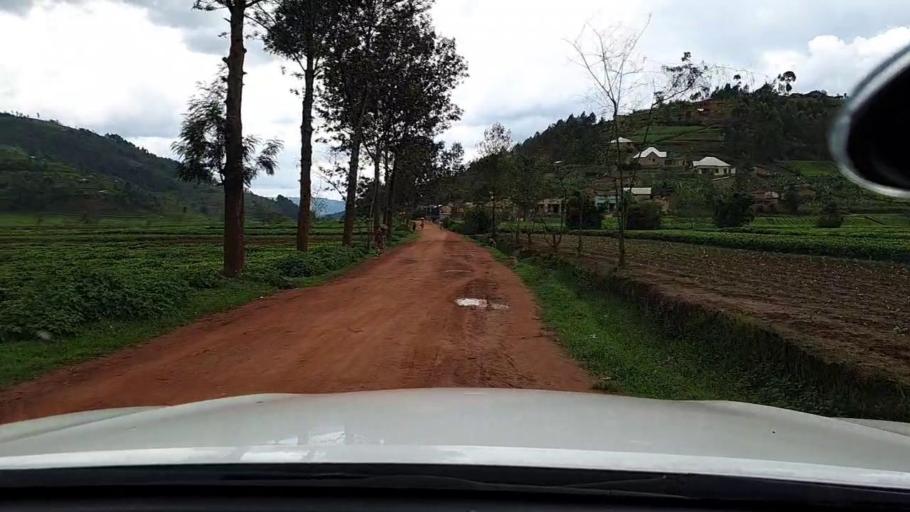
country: RW
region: Northern Province
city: Byumba
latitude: -1.6694
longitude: 29.9250
